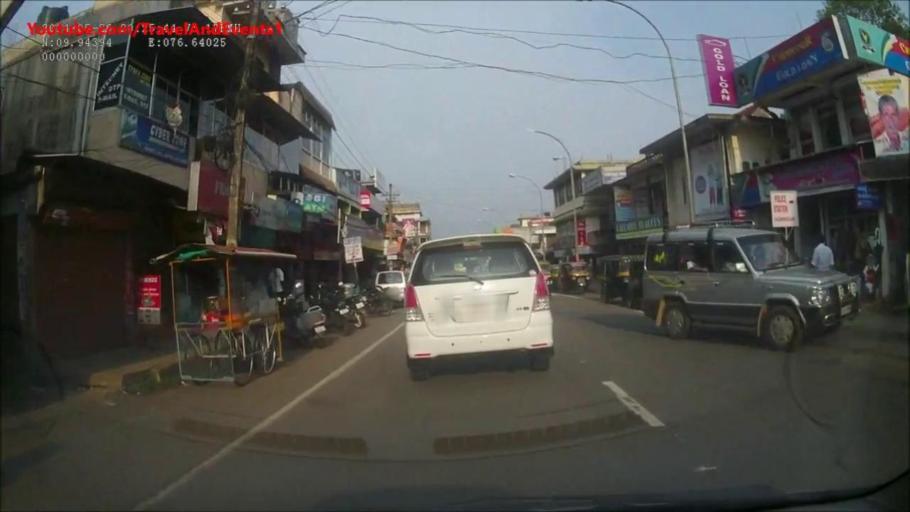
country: IN
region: Kerala
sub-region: Ernakulam
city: Muvattupula
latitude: 9.9399
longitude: 76.6470
